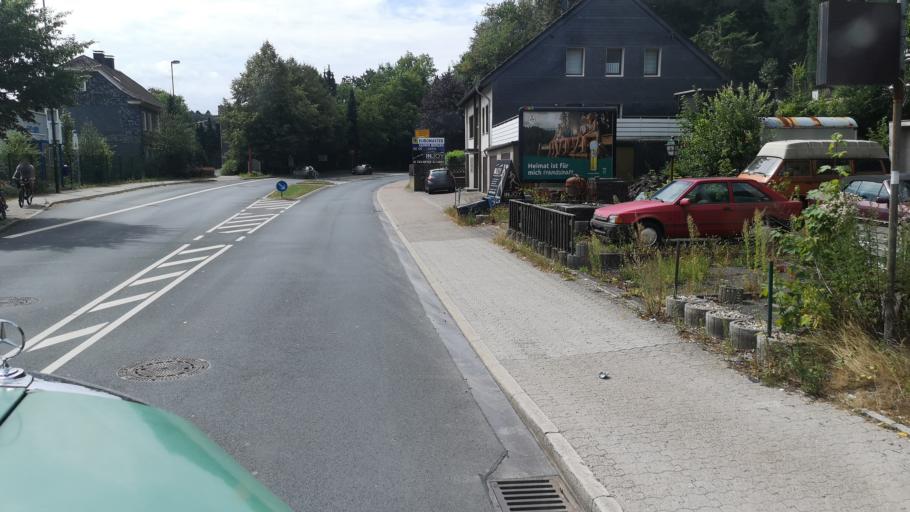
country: DE
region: North Rhine-Westphalia
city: Huckeswagen
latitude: 51.1432
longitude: 7.3507
